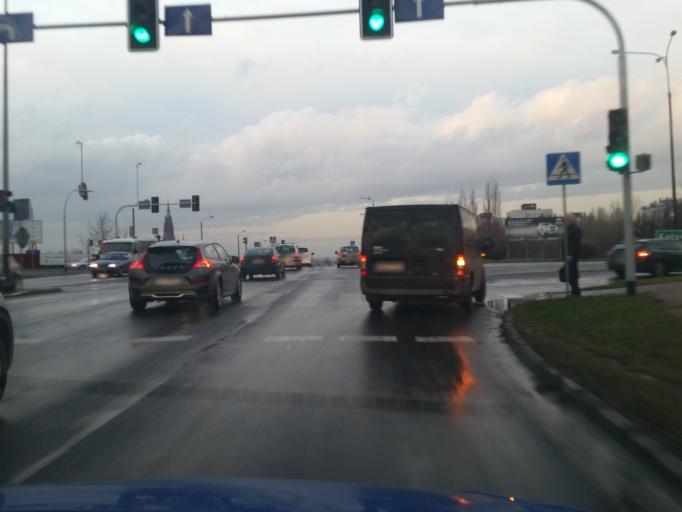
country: PL
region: Silesian Voivodeship
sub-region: Dabrowa Gornicza
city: Dabrowa Gornicza
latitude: 50.3175
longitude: 19.1959
